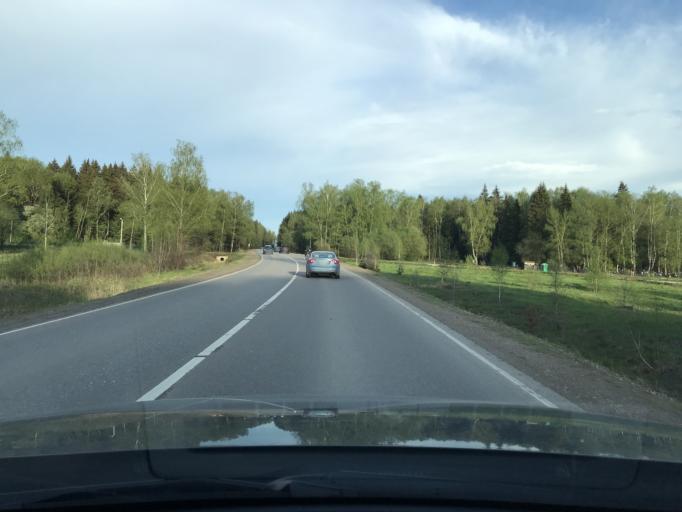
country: RU
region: Moskovskaya
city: Naro-Fominsk
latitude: 55.3457
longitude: 36.7011
